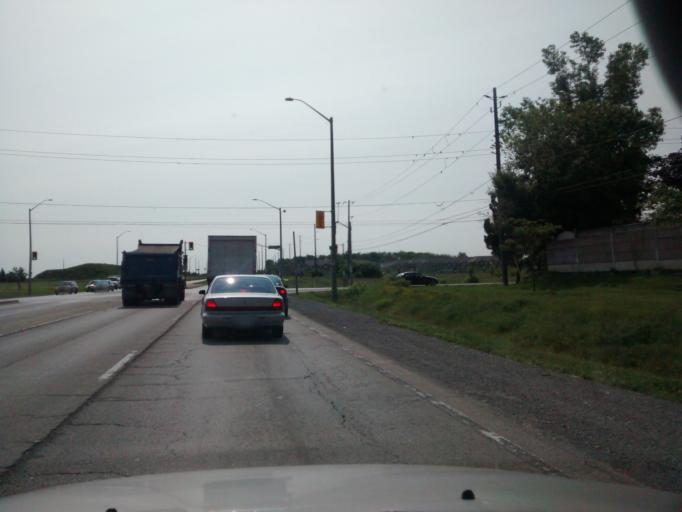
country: CA
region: Ontario
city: Hamilton
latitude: 43.1928
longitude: -79.7802
